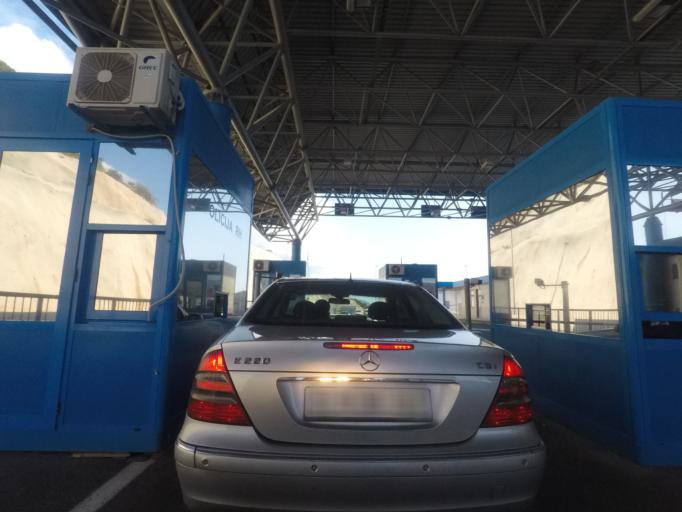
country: BA
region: Federation of Bosnia and Herzegovina
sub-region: Hercegovacko-Bosanski Kanton
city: Neum
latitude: 42.8886
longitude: 17.6527
